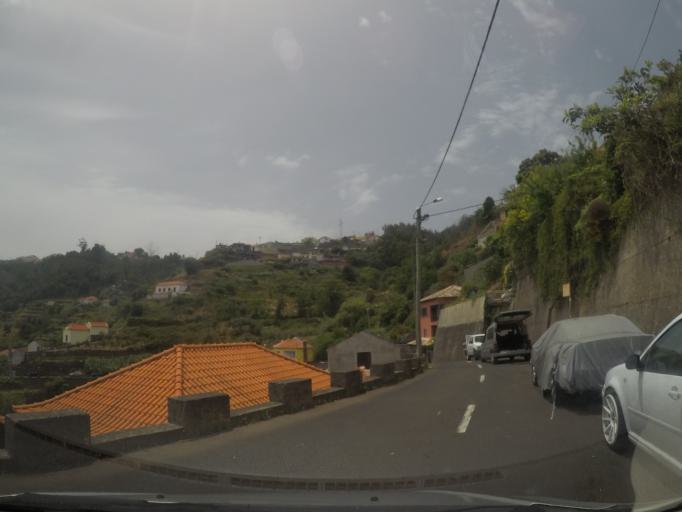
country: PT
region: Madeira
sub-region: Santa Cruz
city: Camacha
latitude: 32.6737
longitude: -16.8382
